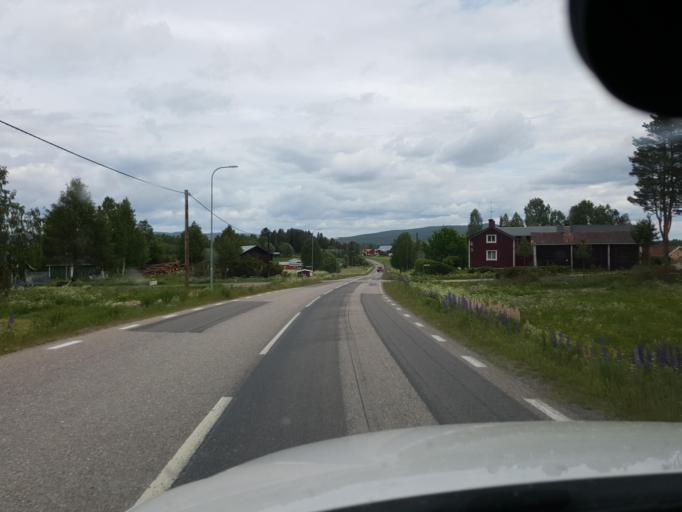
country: SE
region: Gaevleborg
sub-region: Ljusdals Kommun
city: Farila
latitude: 61.8045
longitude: 15.7226
